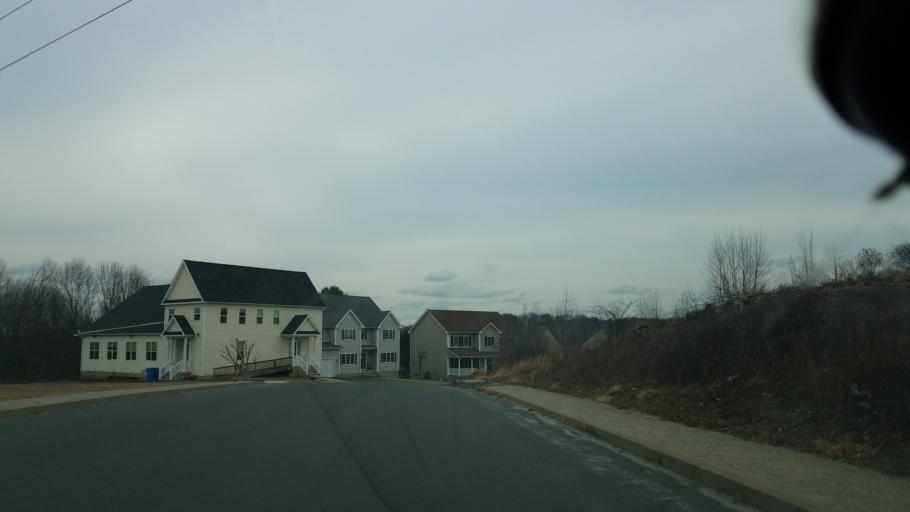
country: US
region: Connecticut
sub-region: New Haven County
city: Waterbury
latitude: 41.5931
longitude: -73.0335
